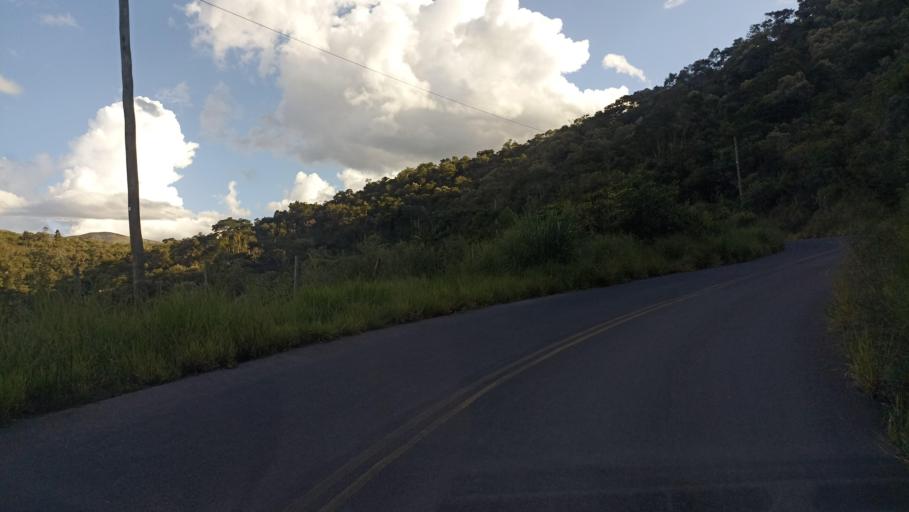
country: BR
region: Minas Gerais
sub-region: Ouro Preto
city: Ouro Preto
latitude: -20.3157
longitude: -43.6163
